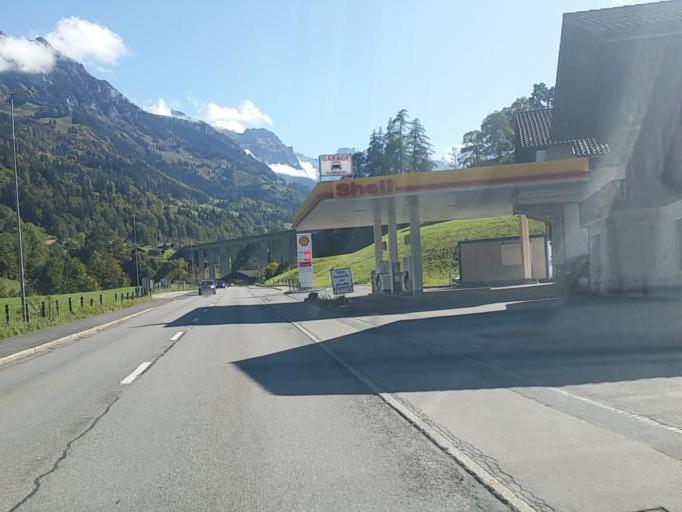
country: CH
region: Bern
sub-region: Frutigen-Niedersimmental District
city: Frutigen
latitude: 46.5785
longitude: 7.6521
